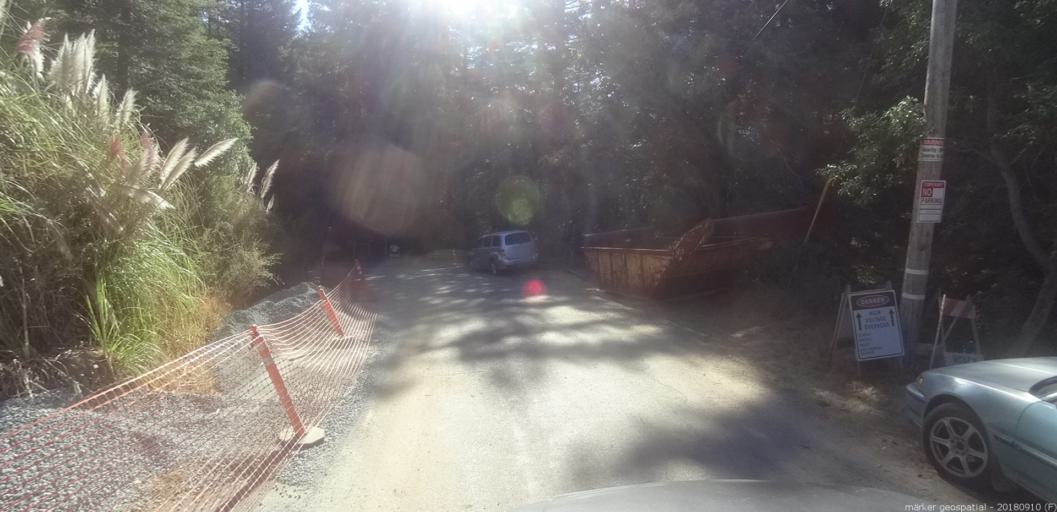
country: US
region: California
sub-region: Monterey County
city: Carmel Valley Village
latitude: 36.3835
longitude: -121.8658
